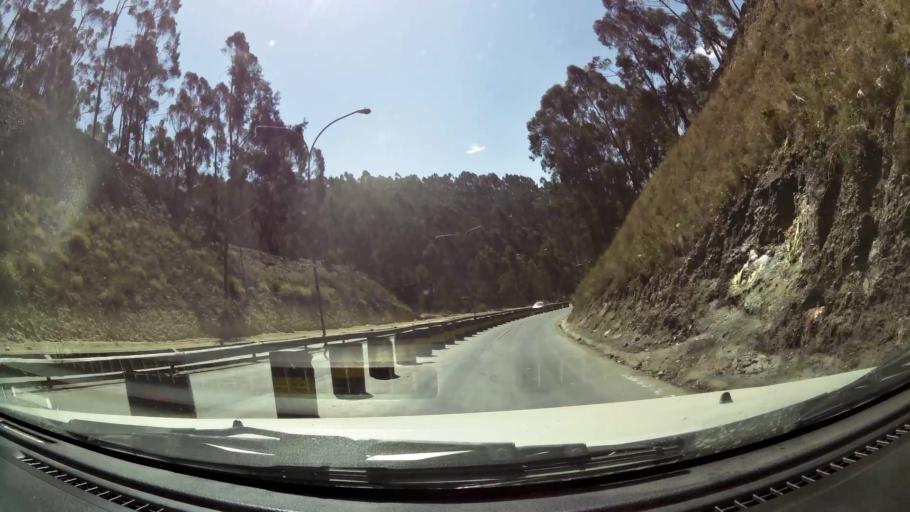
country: BO
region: La Paz
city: La Paz
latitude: -16.4718
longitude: -68.1597
